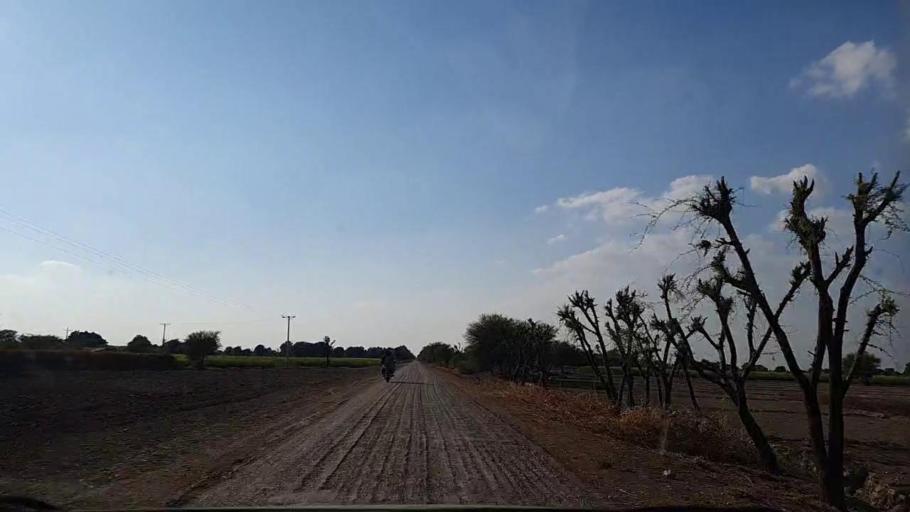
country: PK
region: Sindh
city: Pithoro
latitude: 25.6486
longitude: 69.3065
